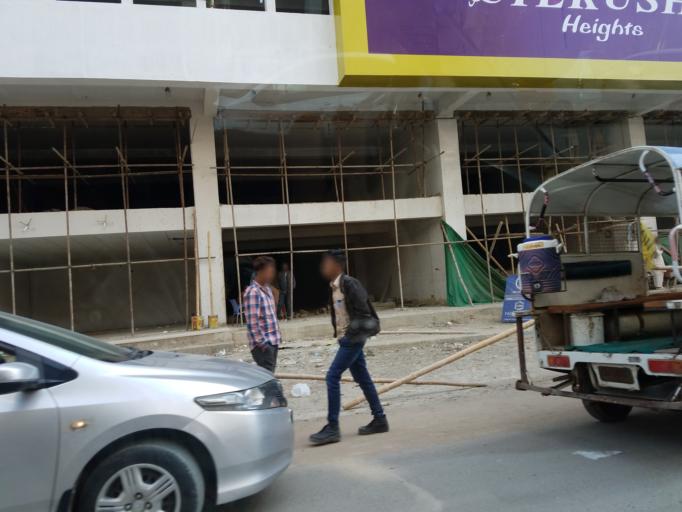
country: PK
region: Sindh
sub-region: Karachi District
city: Karachi
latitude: 24.8783
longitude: 67.0642
